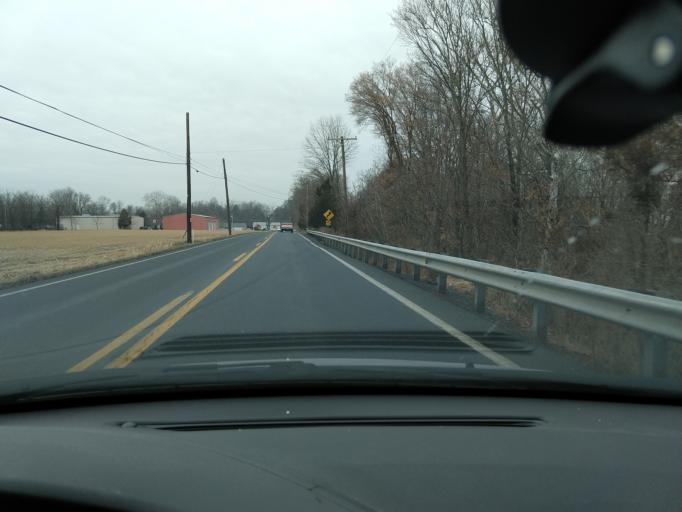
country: US
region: Pennsylvania
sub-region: Montgomery County
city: Stowe
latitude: 40.2447
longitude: -75.7090
